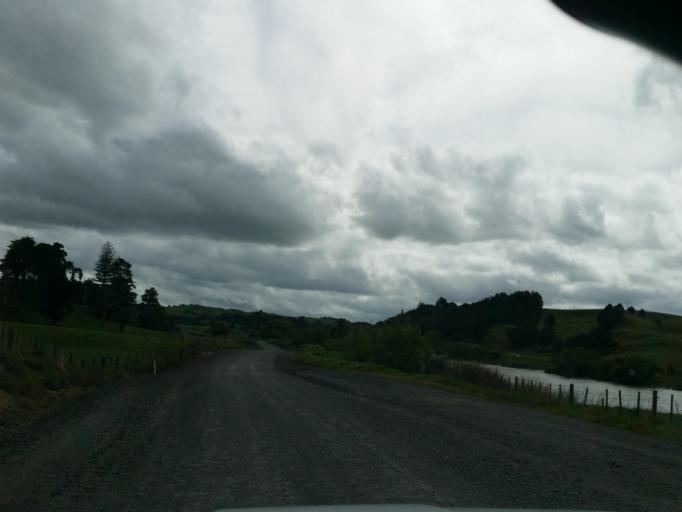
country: NZ
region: Northland
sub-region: Kaipara District
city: Dargaville
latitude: -35.8738
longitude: 174.0327
